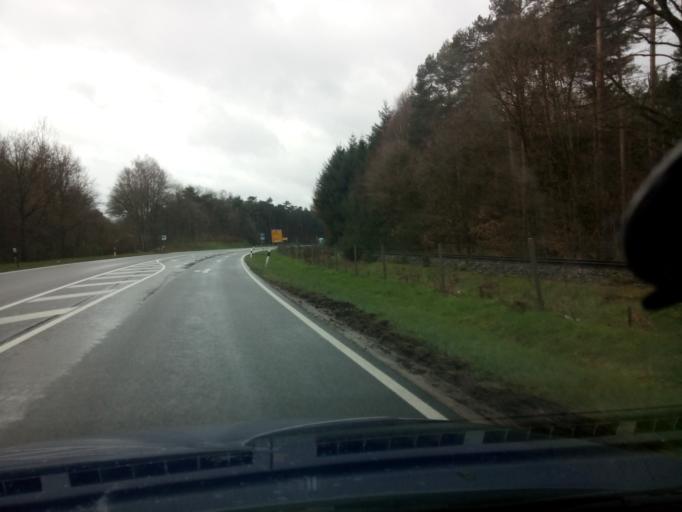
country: DE
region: Lower Saxony
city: Herzlake
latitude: 52.6962
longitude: 7.6231
